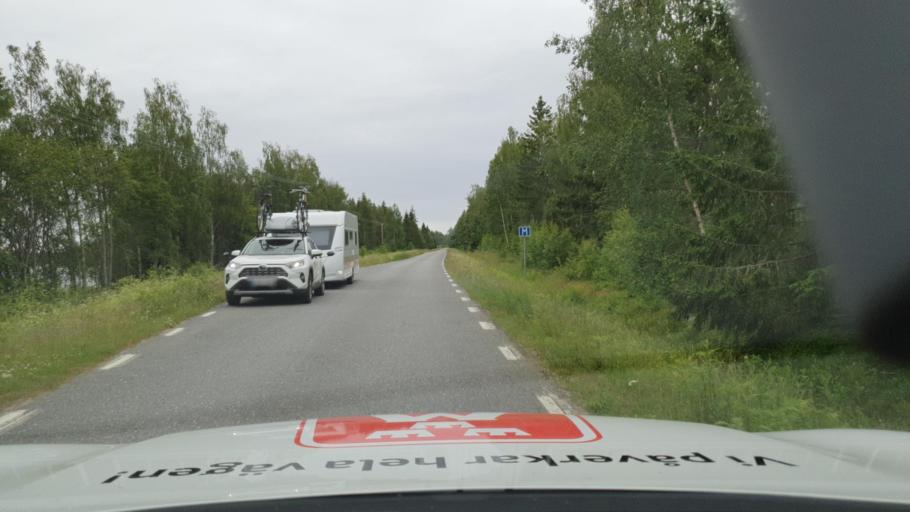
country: SE
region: Vaesterbotten
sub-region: Nordmalings Kommun
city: Nordmaling
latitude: 63.4647
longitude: 19.4653
